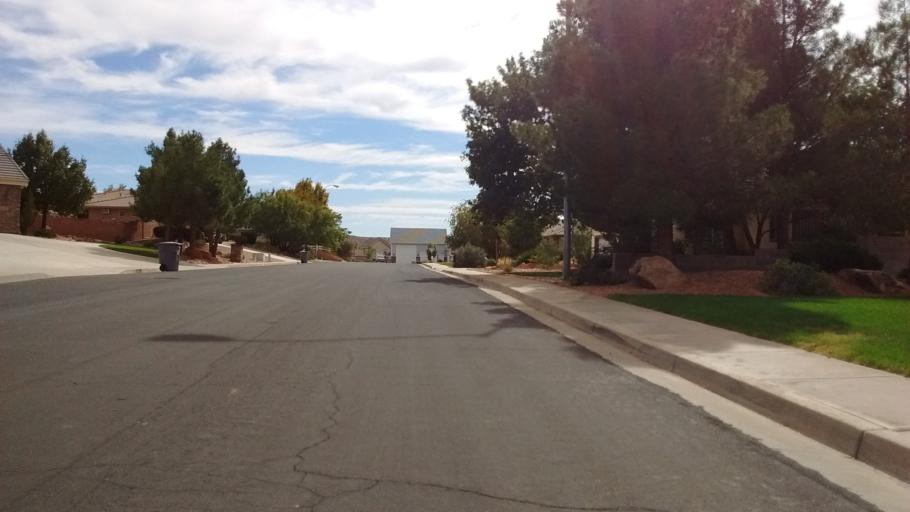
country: US
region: Utah
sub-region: Washington County
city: Washington
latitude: 37.1205
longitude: -113.4952
